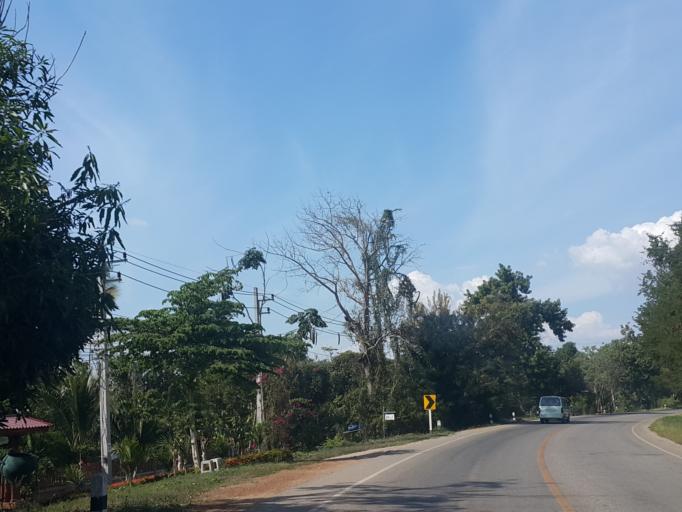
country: TH
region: Sukhothai
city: Sawankhalok
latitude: 17.2688
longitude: 99.8317
